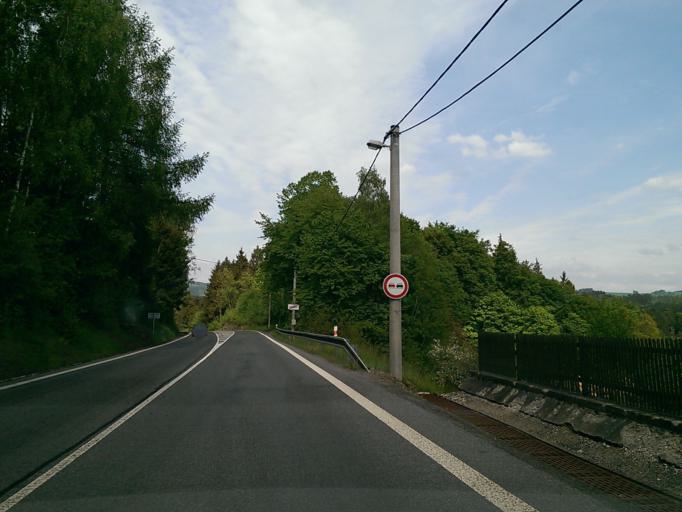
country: CZ
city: Plavy
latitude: 50.6913
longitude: 15.3135
